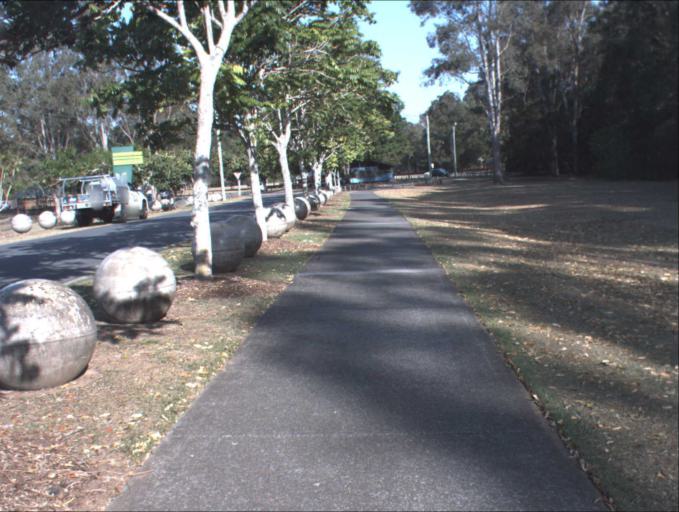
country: AU
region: Queensland
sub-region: Logan
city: Beenleigh
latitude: -27.7002
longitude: 153.1858
